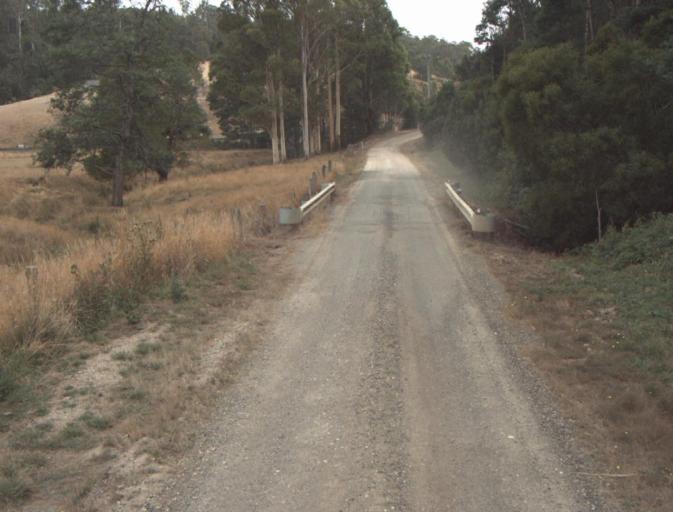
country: AU
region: Tasmania
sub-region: Dorset
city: Bridport
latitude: -41.1808
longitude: 147.2612
